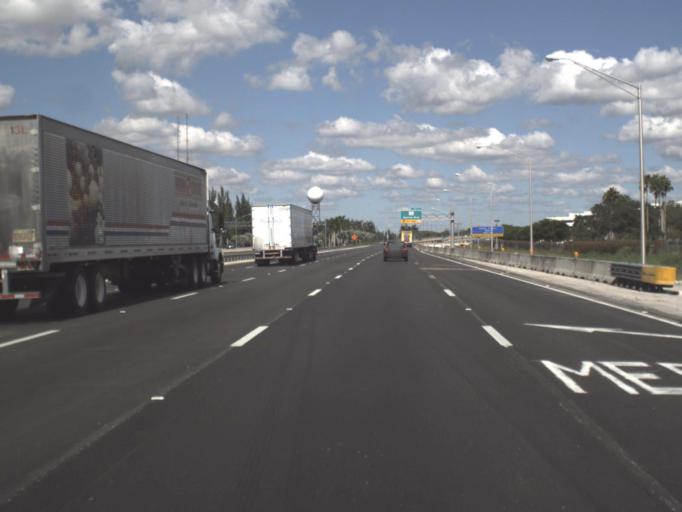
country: US
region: Florida
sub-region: Broward County
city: Weston
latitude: 26.1371
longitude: -80.3434
